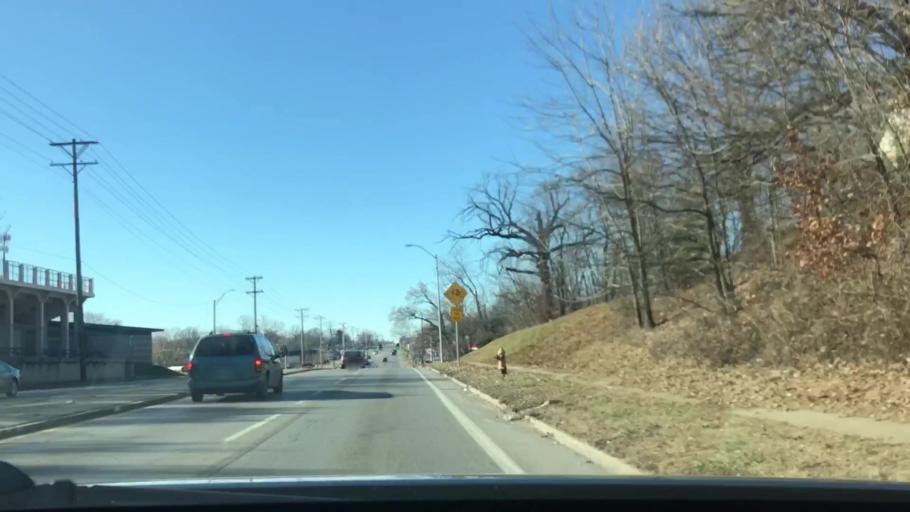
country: US
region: Missouri
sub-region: Jackson County
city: Independence
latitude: 39.0798
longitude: -94.4304
